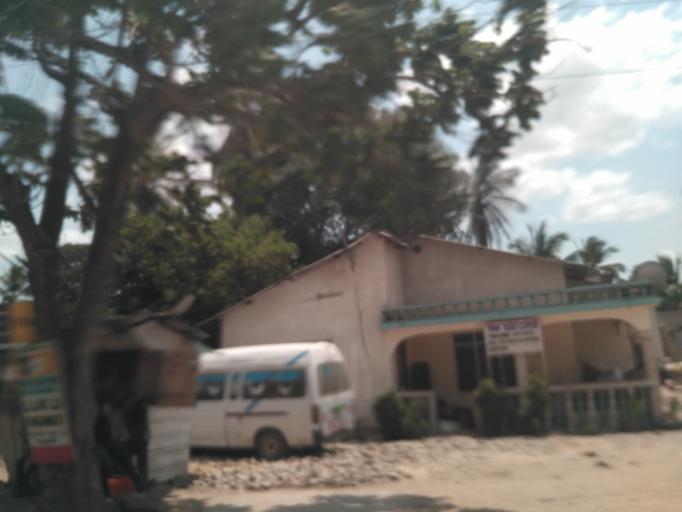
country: TZ
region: Dar es Salaam
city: Dar es Salaam
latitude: -6.8493
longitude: 39.3550
